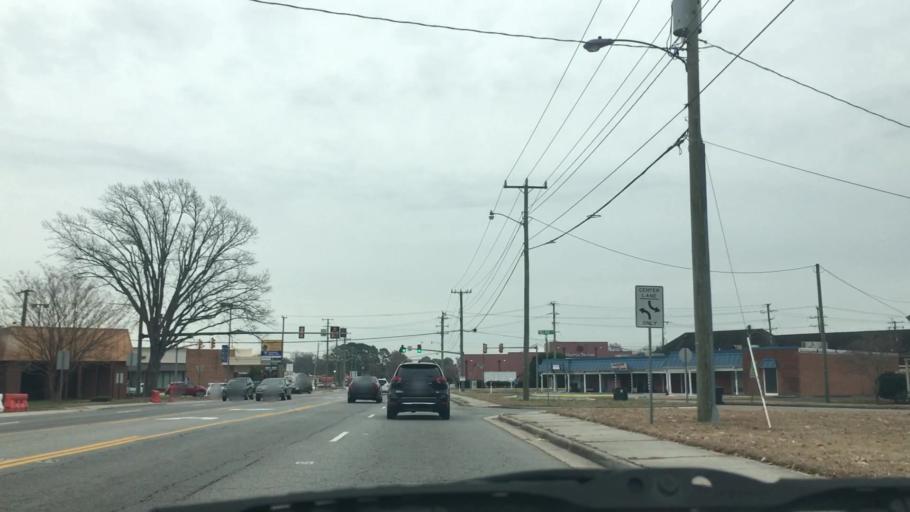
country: US
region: Virginia
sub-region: City of Portsmouth
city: Portsmouth Heights
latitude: 36.8640
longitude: -76.3961
